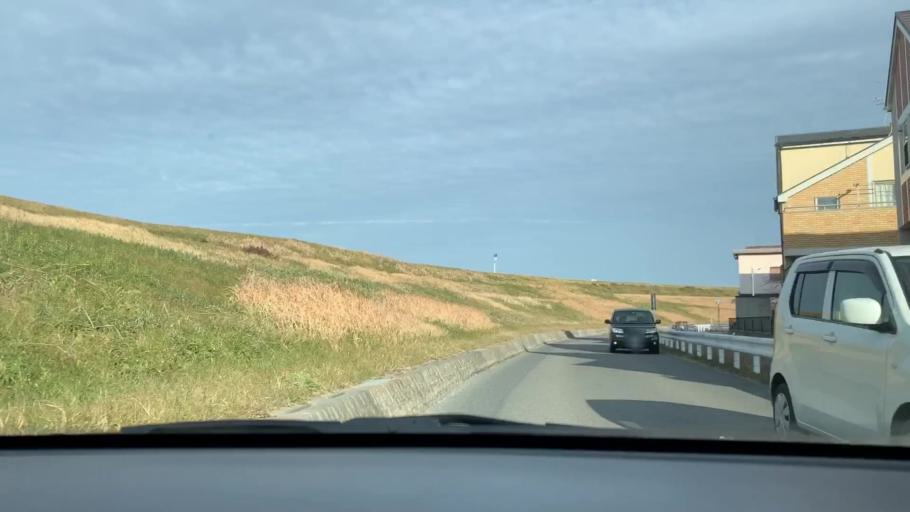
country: JP
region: Chiba
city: Matsudo
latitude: 35.8075
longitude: 139.8908
